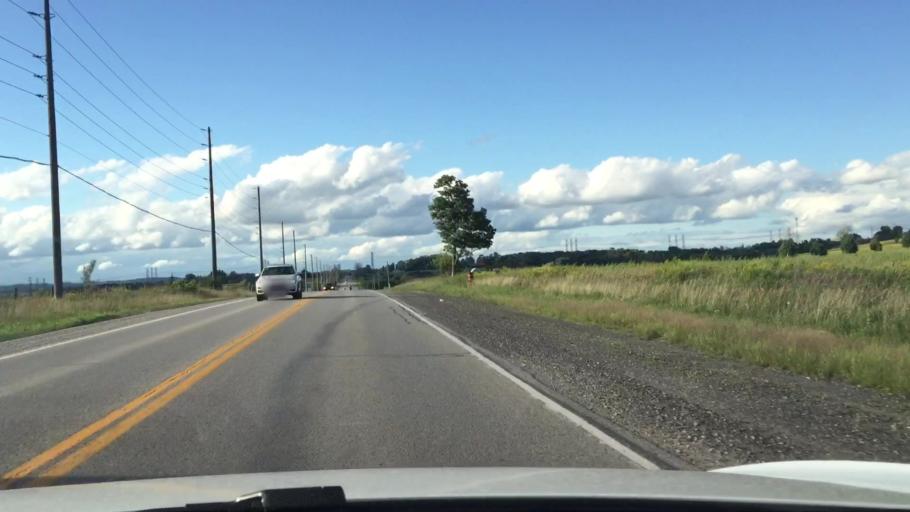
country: CA
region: Ontario
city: Oshawa
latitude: 43.9614
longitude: -78.8591
